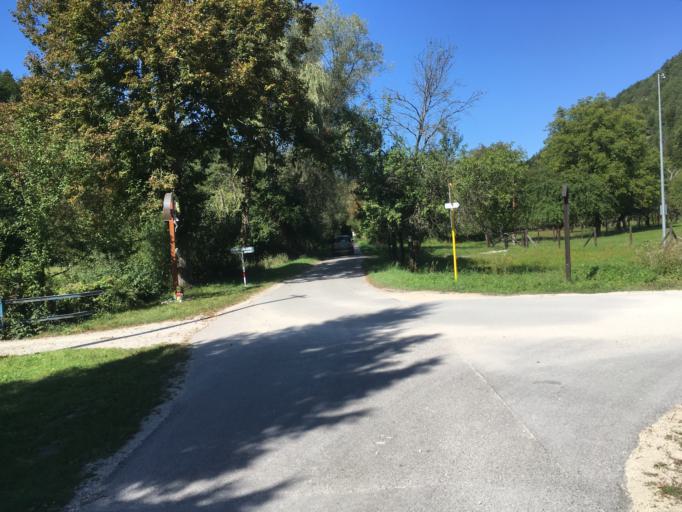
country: SK
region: Trenciansky
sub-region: Okres Povazska Bystrica
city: Povazska Bystrica
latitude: 49.0169
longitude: 18.4407
